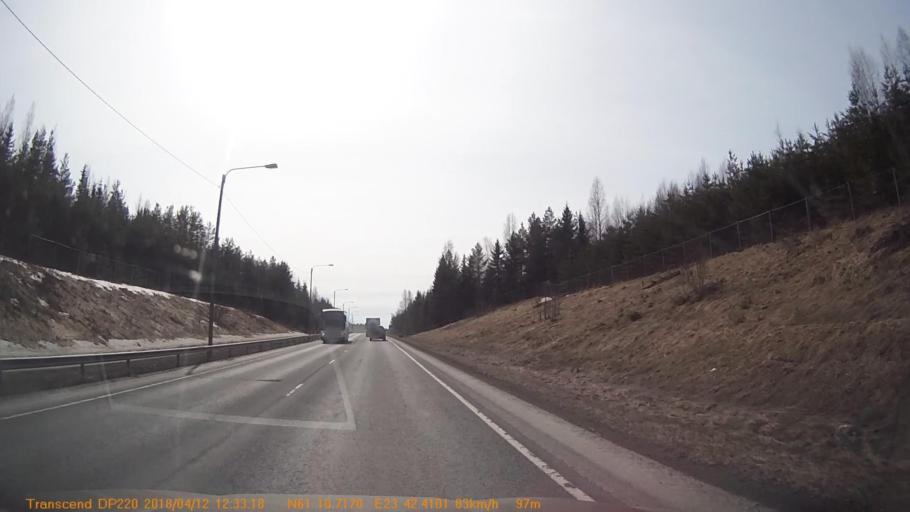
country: FI
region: Pirkanmaa
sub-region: Etelae-Pirkanmaa
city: Kylmaekoski
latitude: 61.1782
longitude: 23.7066
